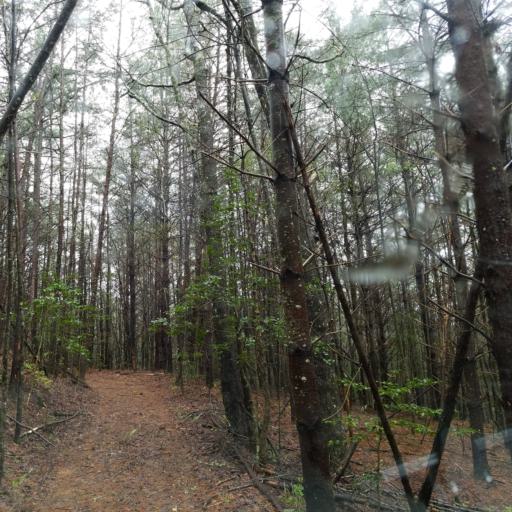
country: US
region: Georgia
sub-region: Fannin County
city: Blue Ridge
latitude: 34.8364
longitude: -84.2374
